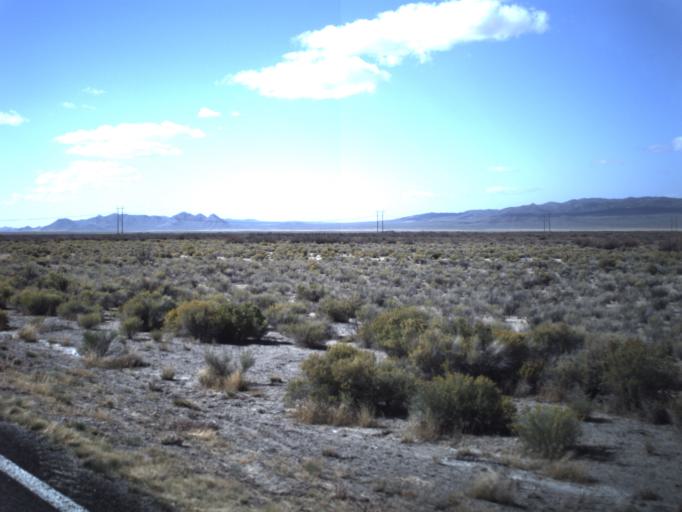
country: US
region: Utah
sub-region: Beaver County
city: Milford
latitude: 38.5797
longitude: -112.9892
